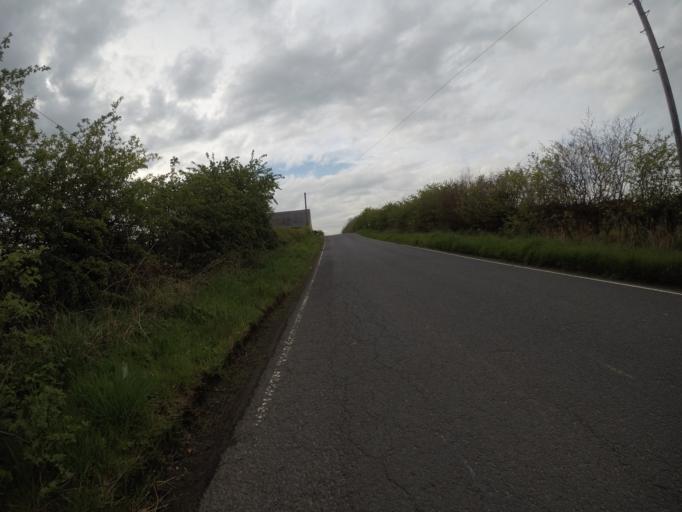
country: GB
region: Scotland
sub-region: East Ayrshire
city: Kilmarnock
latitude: 55.6424
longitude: -4.4788
